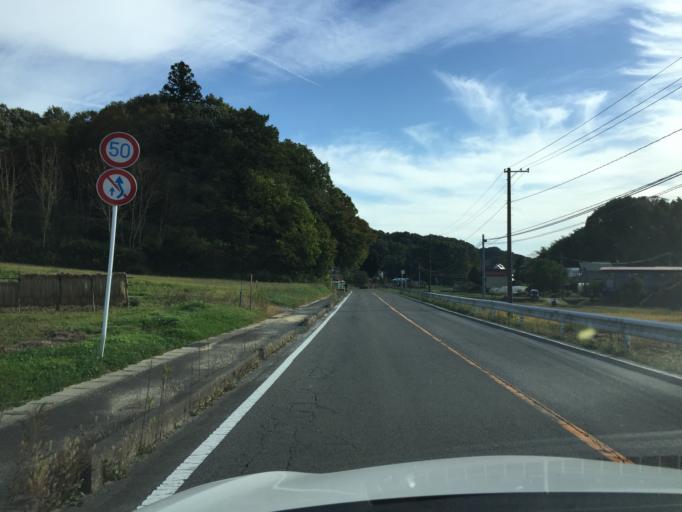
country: JP
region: Fukushima
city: Miharu
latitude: 37.4189
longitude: 140.4611
